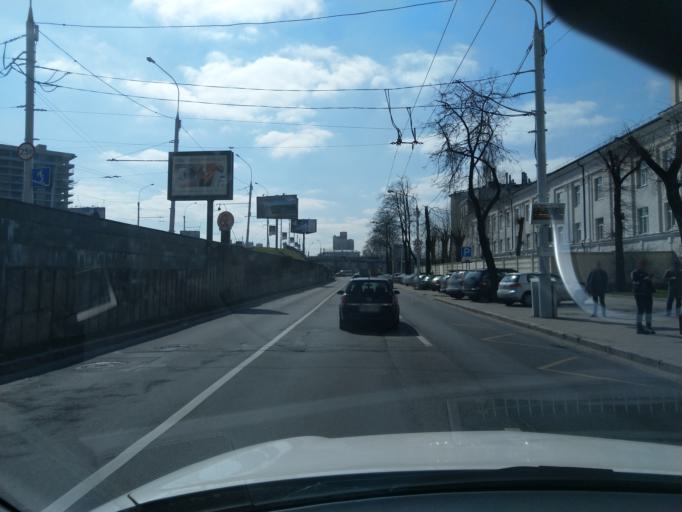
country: BY
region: Minsk
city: Minsk
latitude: 53.8864
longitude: 27.5374
